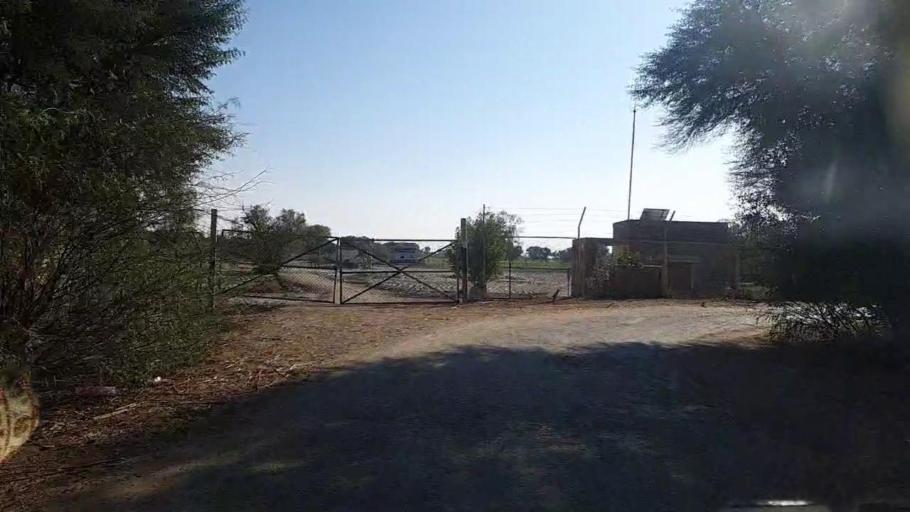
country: PK
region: Sindh
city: Khairpur
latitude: 27.9143
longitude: 69.7519
